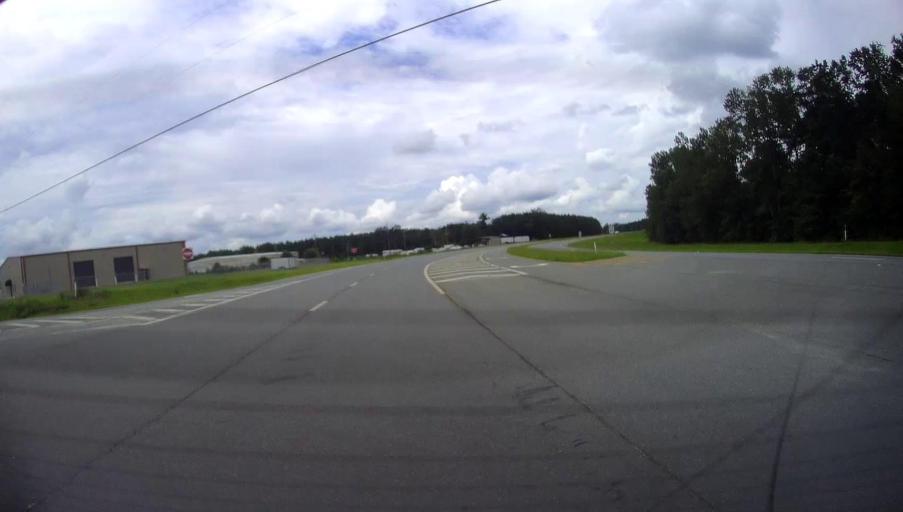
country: US
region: Georgia
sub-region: Schley County
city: Ellaville
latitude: 32.2274
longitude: -84.2930
